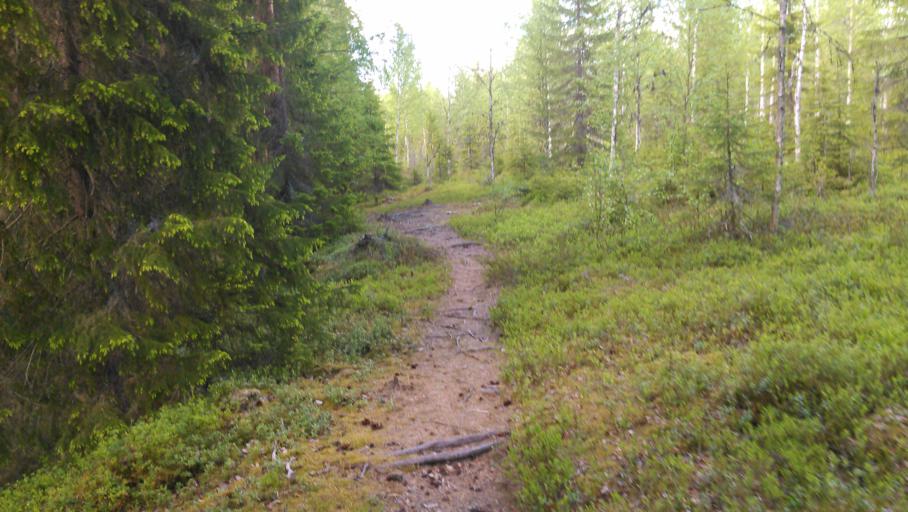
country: SE
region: Vaesterbotten
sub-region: Vannas Kommun
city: Vannasby
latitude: 64.0158
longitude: 19.9033
